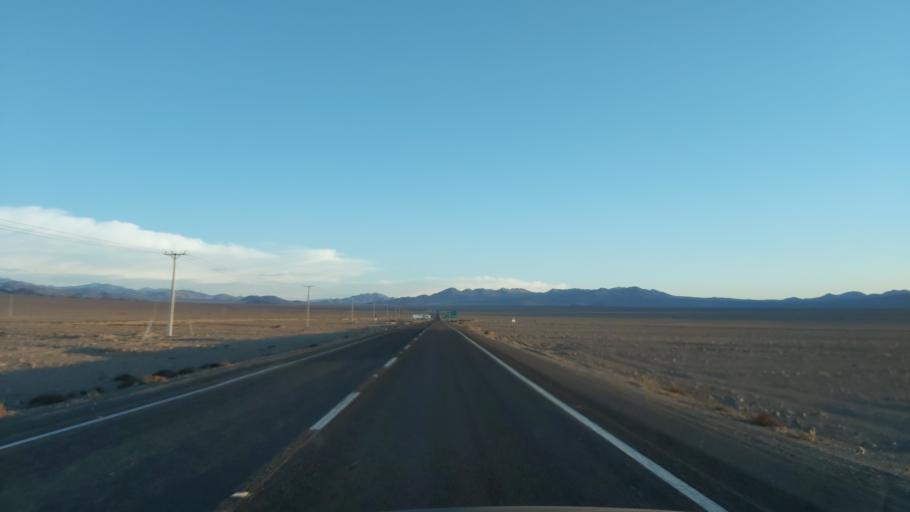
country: CL
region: Atacama
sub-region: Provincia de Chanaral
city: Diego de Almagro
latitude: -26.6254
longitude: -69.9507
